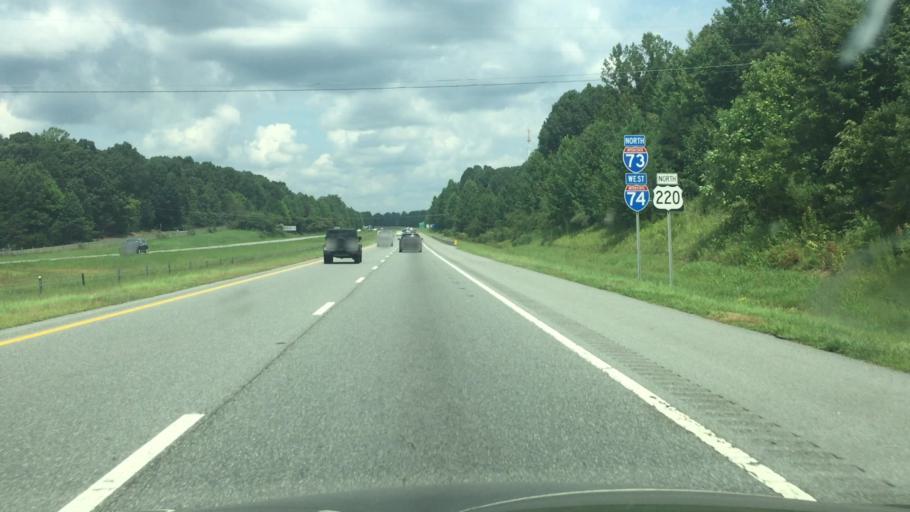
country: US
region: North Carolina
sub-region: Randolph County
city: Asheboro
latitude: 35.5999
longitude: -79.8180
